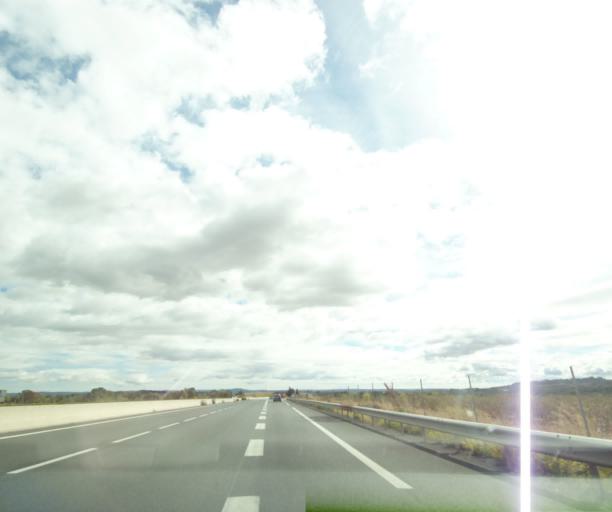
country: FR
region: Languedoc-Roussillon
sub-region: Departement de l'Herault
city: Nebian
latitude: 43.6590
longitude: 3.4433
